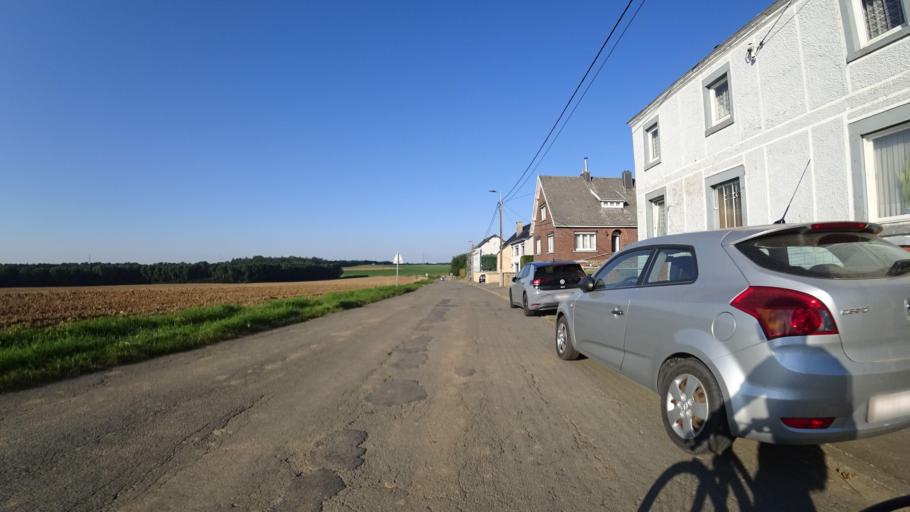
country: BE
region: Wallonia
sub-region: Province de Namur
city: Namur
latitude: 50.4954
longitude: 4.8484
